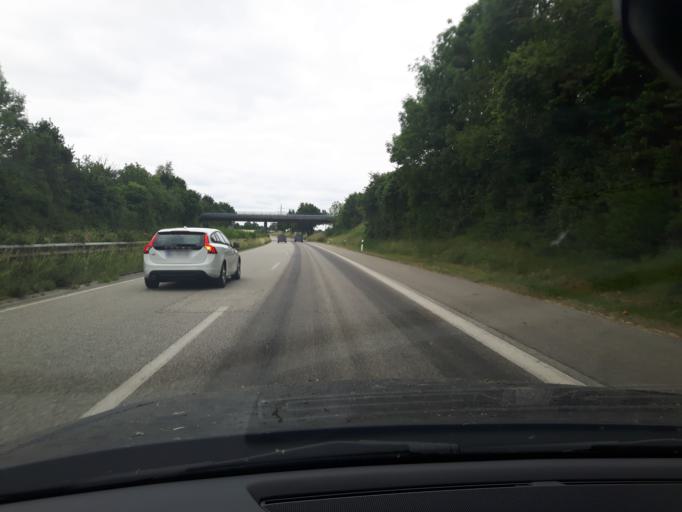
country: DE
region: Schleswig-Holstein
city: Travemuende
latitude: 53.9615
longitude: 10.8401
